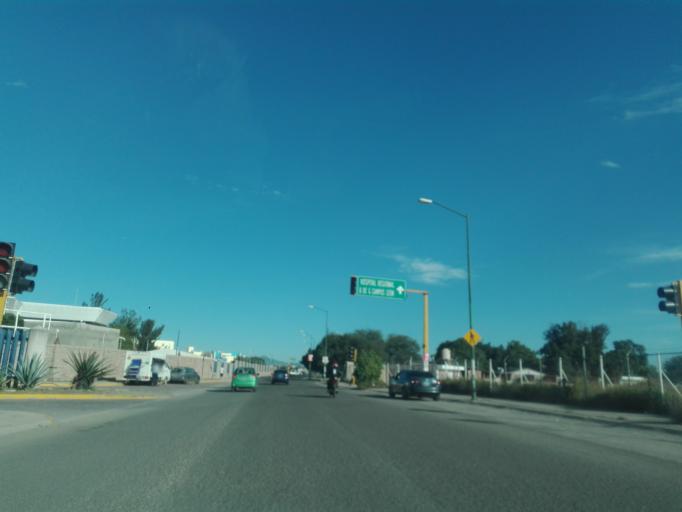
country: MX
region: Guanajuato
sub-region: Leon
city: Ladrilleras del Refugio
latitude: 21.0626
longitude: -101.5819
